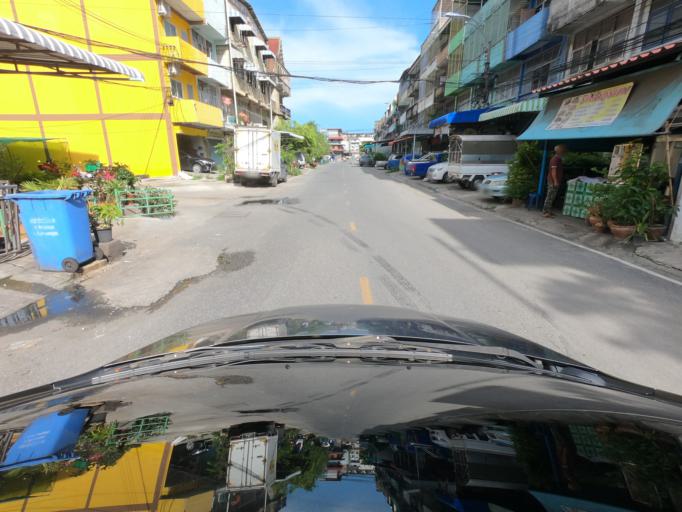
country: TH
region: Bangkok
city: Phra Khanong
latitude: 13.6524
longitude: 100.5943
